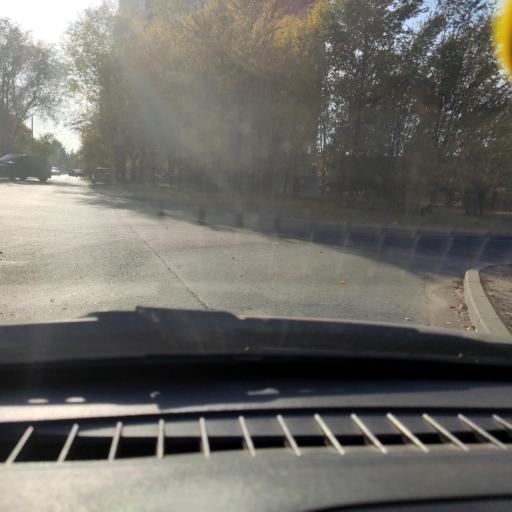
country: RU
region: Samara
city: Tol'yatti
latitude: 53.5167
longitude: 49.3140
